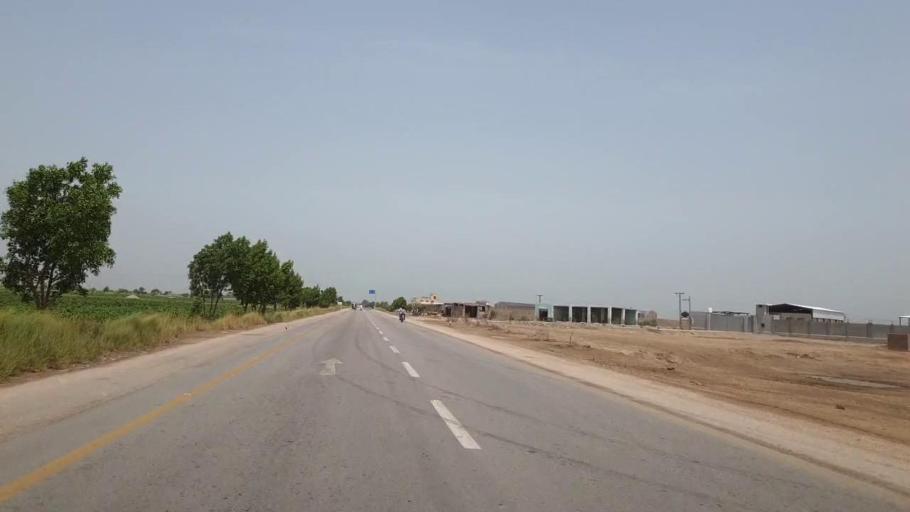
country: PK
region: Sindh
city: Nawabshah
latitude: 26.2297
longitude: 68.4867
